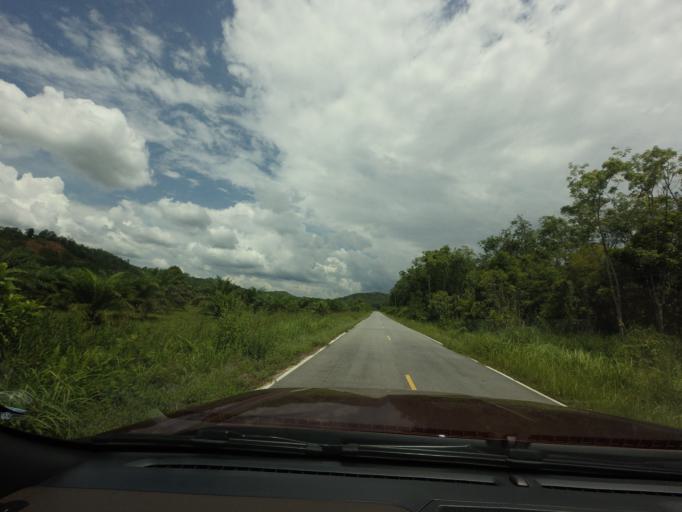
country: TH
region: Narathiwat
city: Chanae
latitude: 6.0597
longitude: 101.6877
